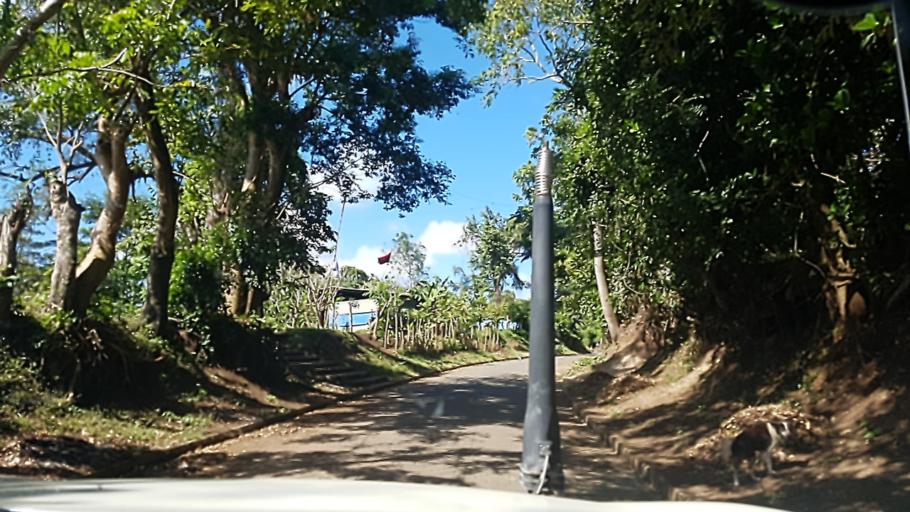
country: NI
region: Carazo
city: La Paz de Oriente
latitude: 11.8265
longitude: -86.1491
